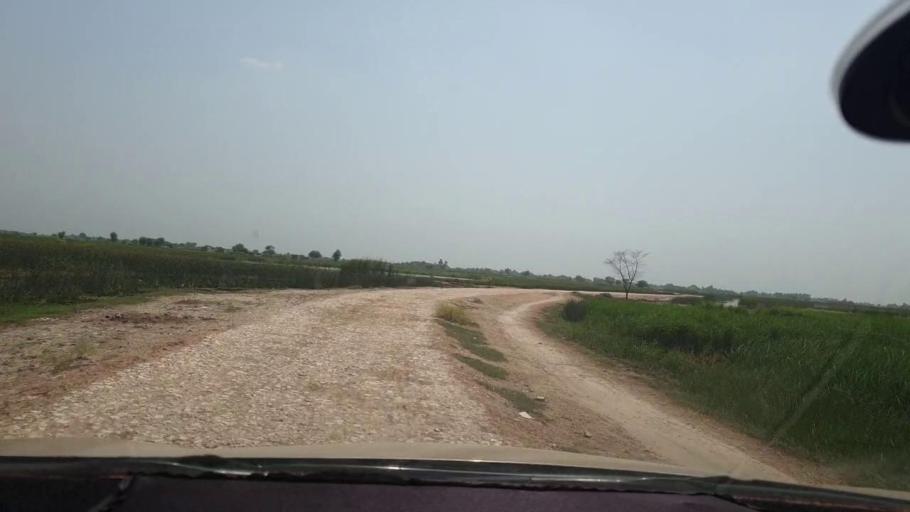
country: PK
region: Sindh
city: Kambar
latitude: 27.6507
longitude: 67.9324
